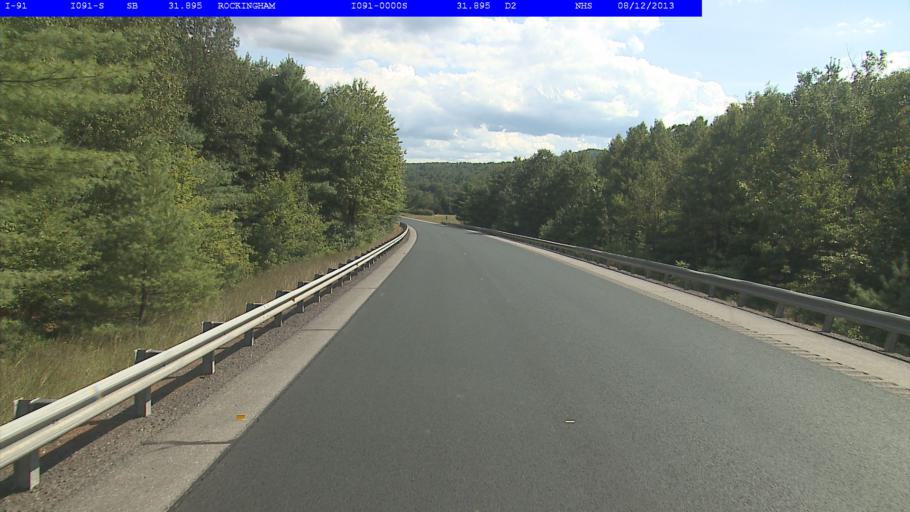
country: US
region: Vermont
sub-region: Windham County
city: Bellows Falls
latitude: 43.1338
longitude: -72.4770
